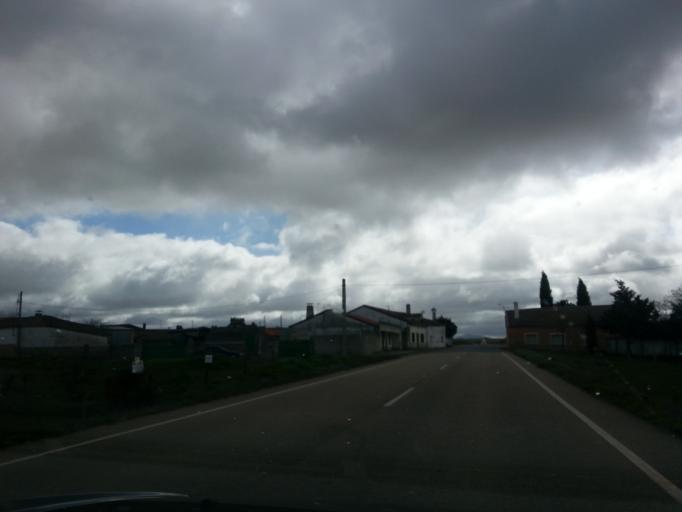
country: ES
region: Castille and Leon
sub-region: Provincia de Salamanca
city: La Fuente de San Esteban
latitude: 40.7774
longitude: -6.2300
